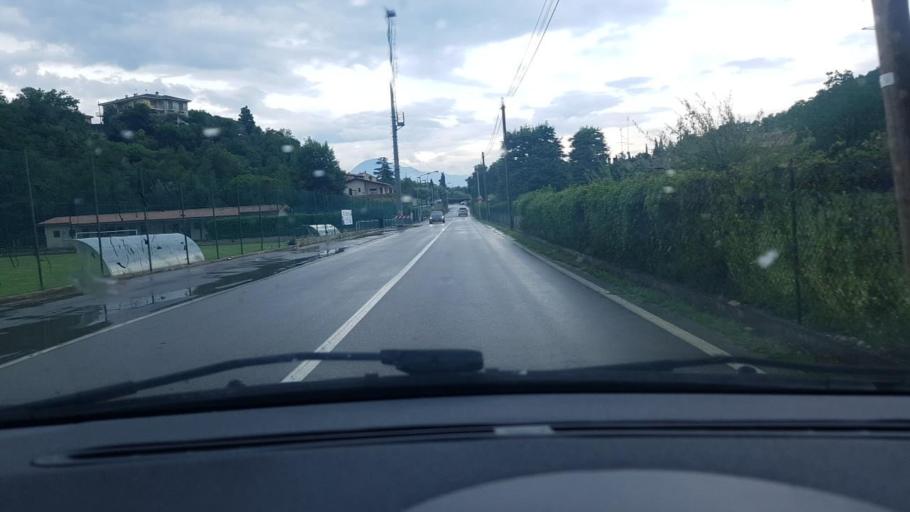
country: IT
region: Veneto
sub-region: Provincia di Verona
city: Torri del Benaco
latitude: 45.6018
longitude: 10.7001
